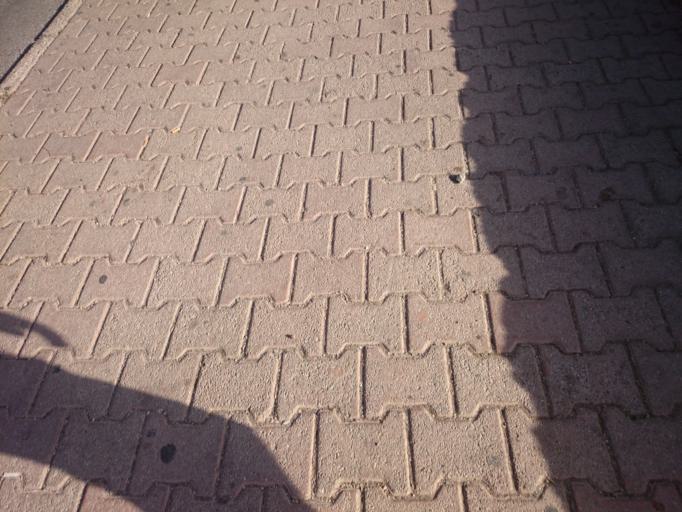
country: ME
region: Kotor
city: Kotor
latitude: 42.4293
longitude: 18.7684
